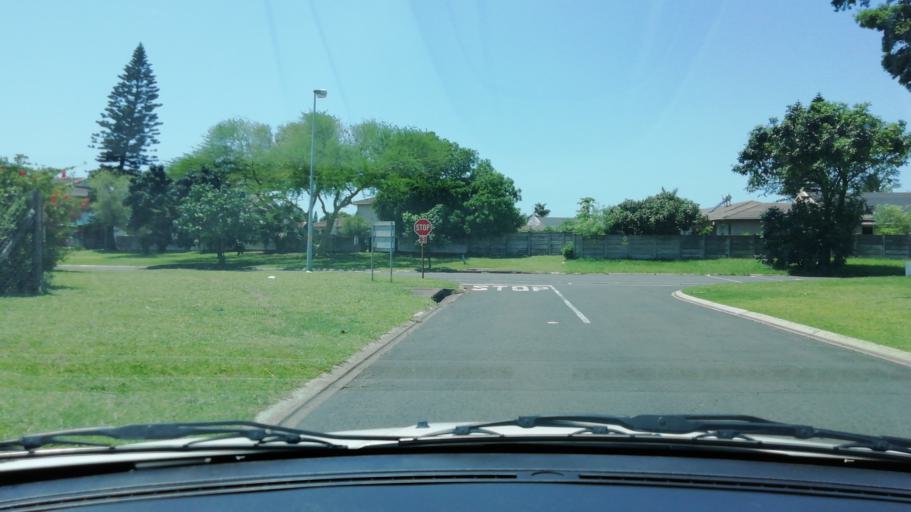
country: ZA
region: KwaZulu-Natal
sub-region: uThungulu District Municipality
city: Richards Bay
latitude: -28.7364
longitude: 32.0479
